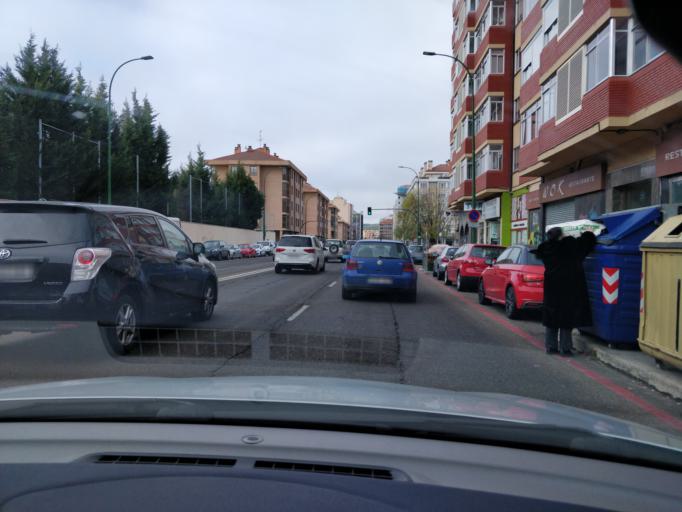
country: ES
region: Castille and Leon
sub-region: Provincia de Burgos
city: Burgos
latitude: 42.3477
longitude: -3.6695
